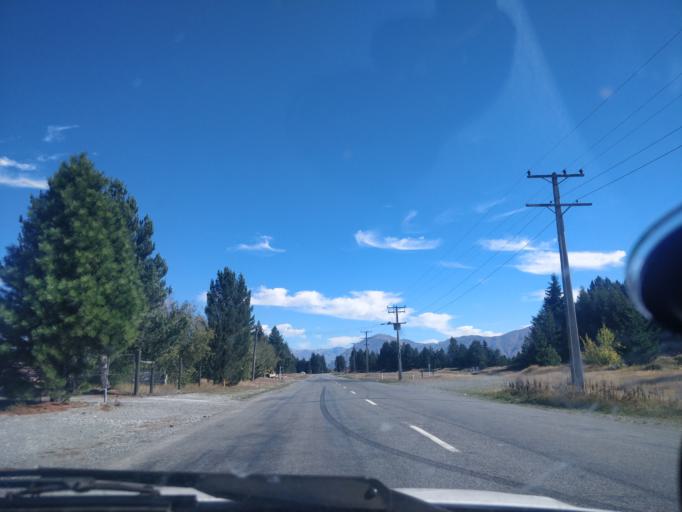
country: NZ
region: Otago
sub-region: Queenstown-Lakes District
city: Wanaka
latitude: -44.2648
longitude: 170.0856
